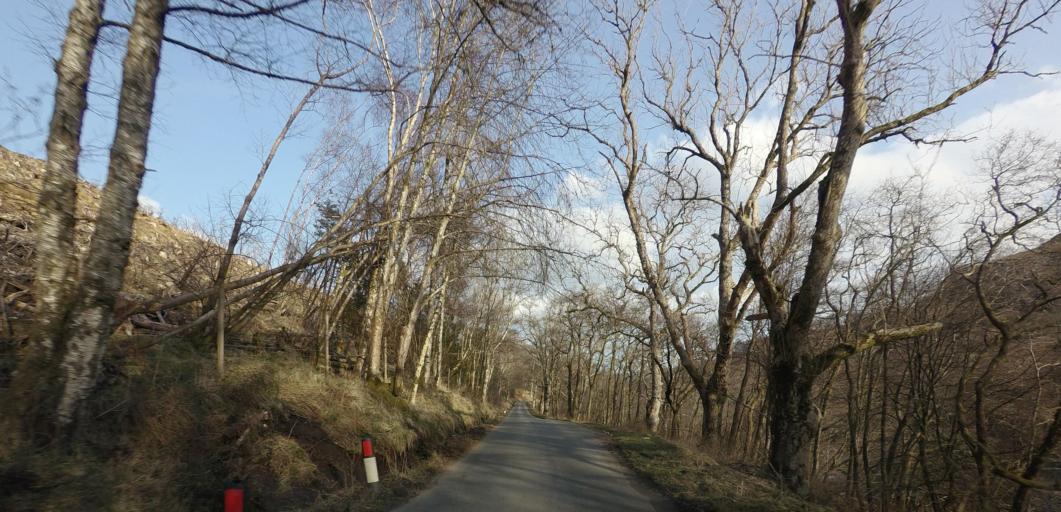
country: GB
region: Scotland
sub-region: Perth and Kinross
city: Aberfeldy
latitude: 56.6045
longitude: -4.0877
